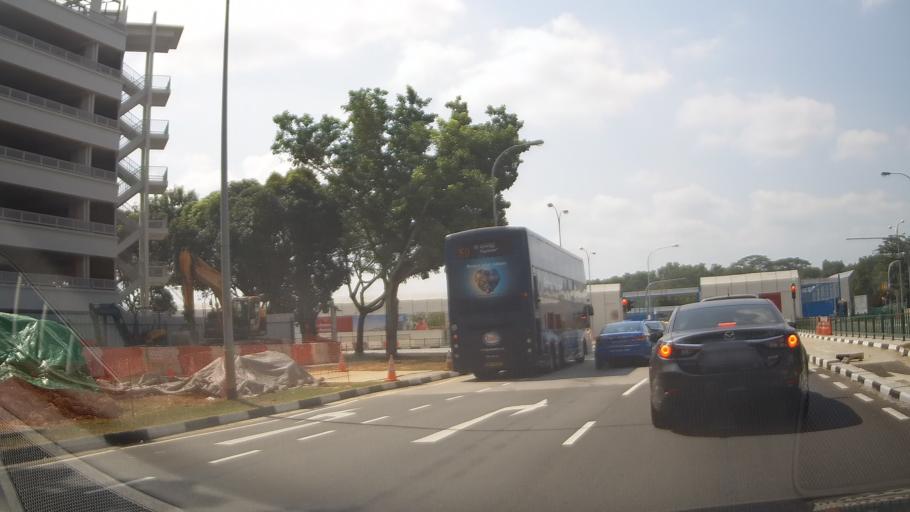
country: MY
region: Johor
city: Kampung Pasir Gudang Baru
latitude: 1.3871
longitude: 103.9072
